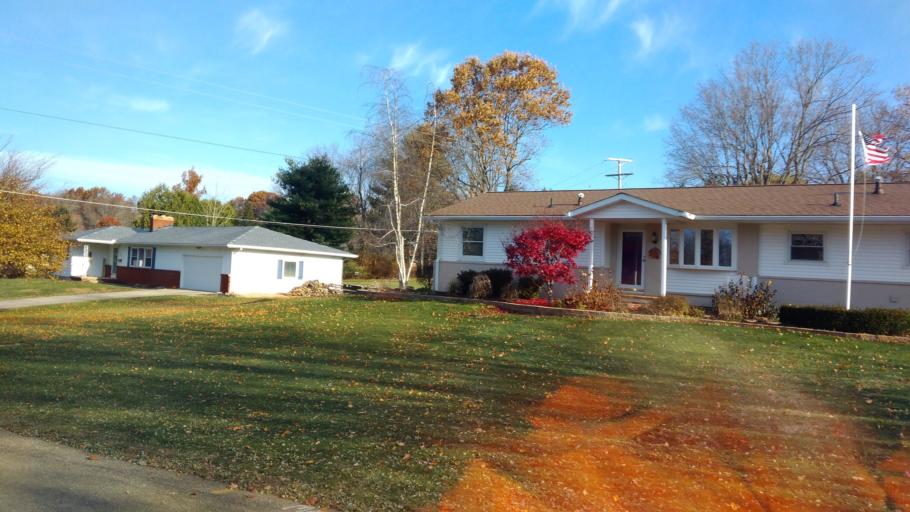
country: US
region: Ohio
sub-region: Richland County
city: Lexington
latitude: 40.6906
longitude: -82.5385
